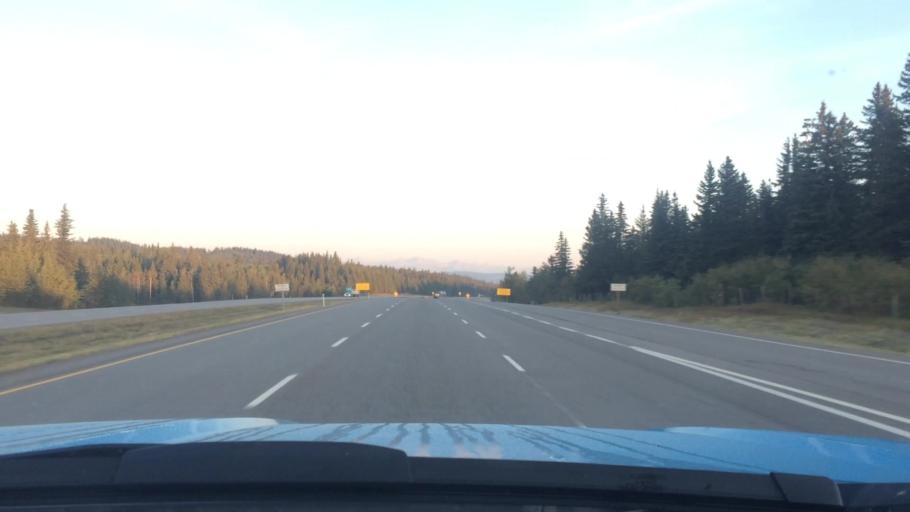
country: CA
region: Alberta
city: Cochrane
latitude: 51.1461
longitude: -114.7311
